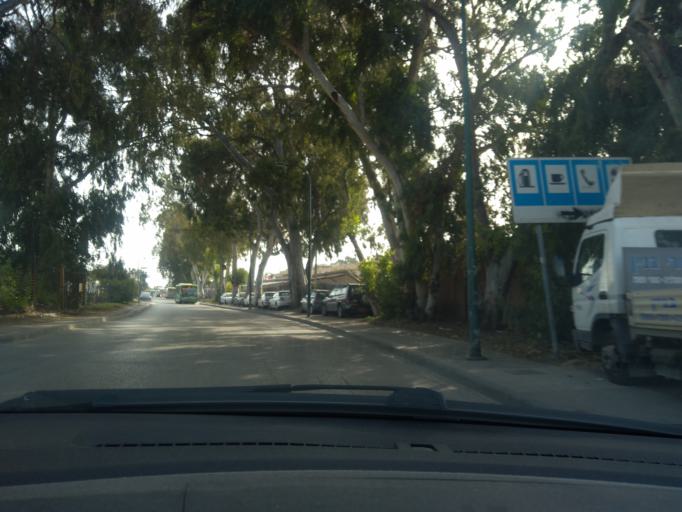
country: IL
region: Central District
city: Netanya
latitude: 32.3226
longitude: 34.8684
